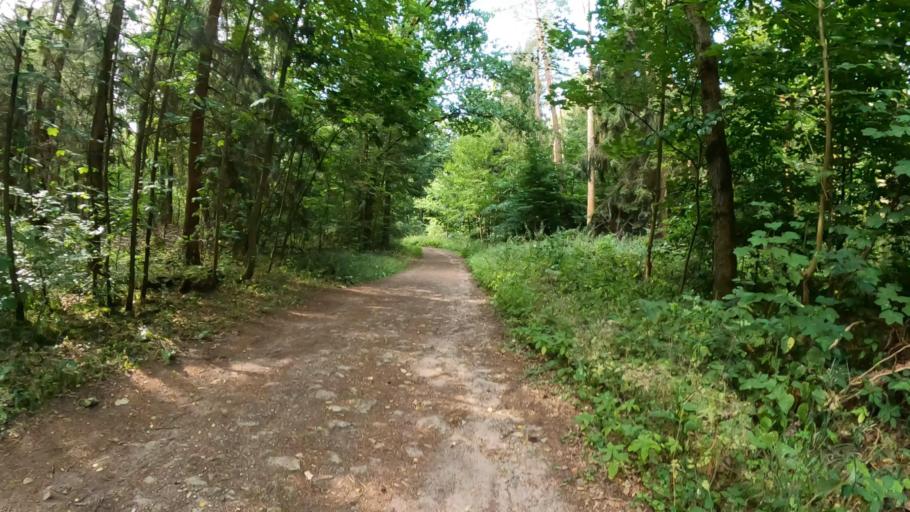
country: DE
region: Schleswig-Holstein
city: Geesthacht
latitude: 53.4264
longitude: 10.3944
